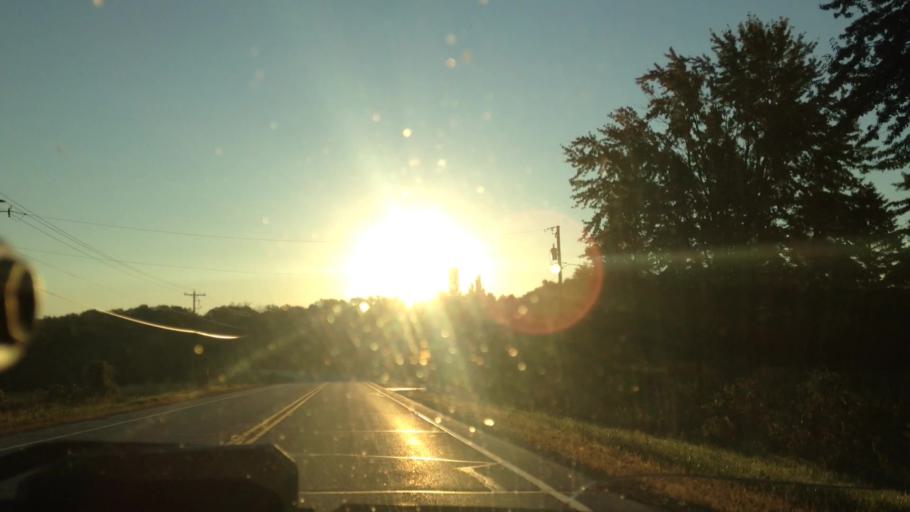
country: US
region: Wisconsin
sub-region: Washington County
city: Newburg
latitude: 43.4232
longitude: -88.0668
